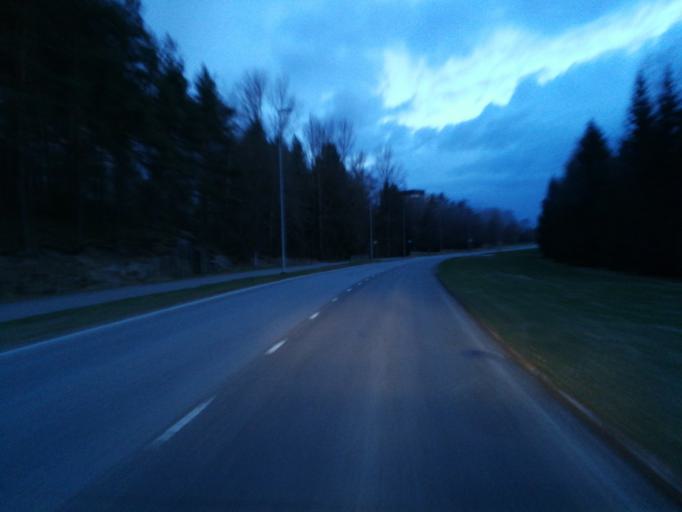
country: FI
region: Varsinais-Suomi
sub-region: Turku
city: Turku
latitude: 60.4666
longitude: 22.2220
